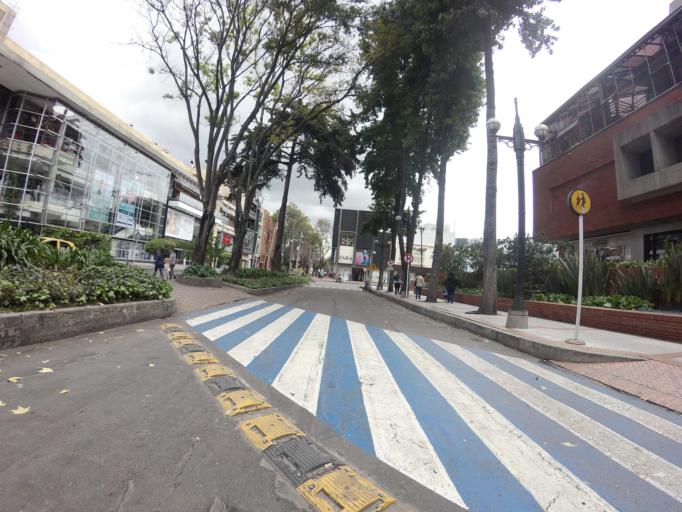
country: CO
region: Bogota D.C.
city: Barrio San Luis
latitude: 4.6672
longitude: -74.0538
